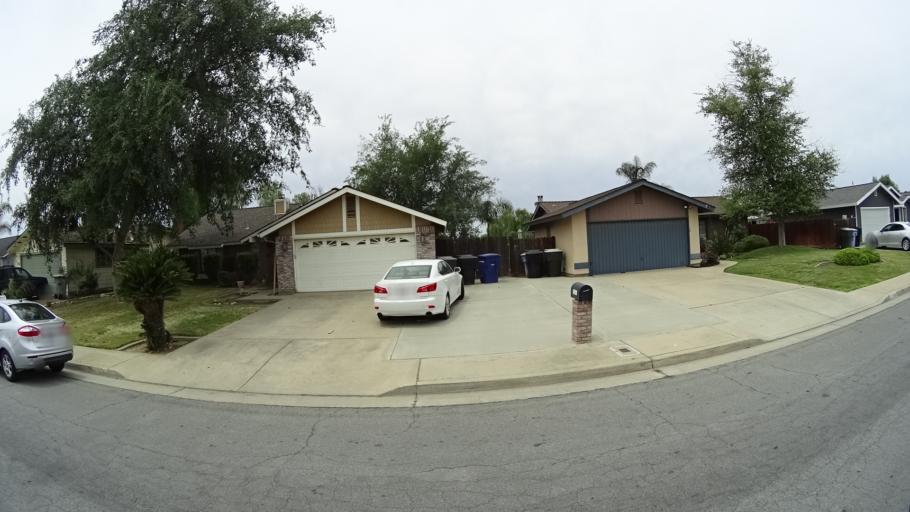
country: US
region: California
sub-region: Kings County
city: Hanford
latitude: 36.3511
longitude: -119.6320
